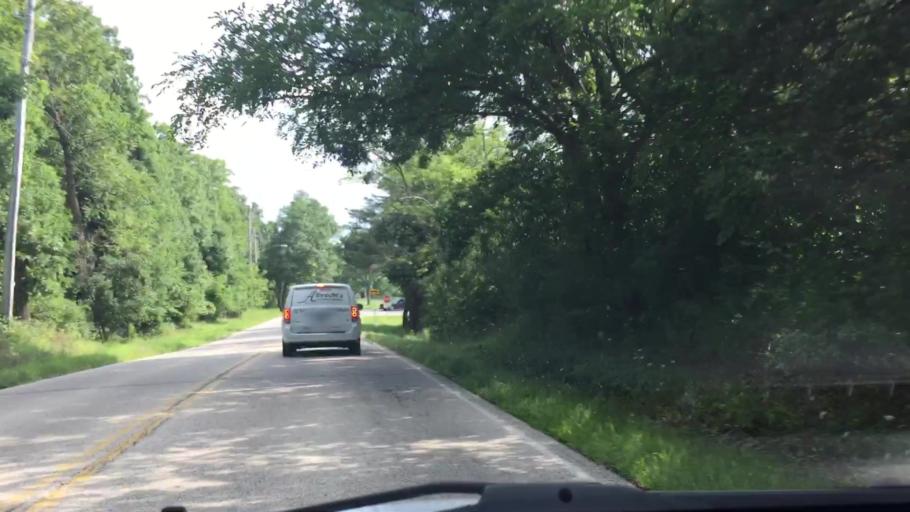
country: US
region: Wisconsin
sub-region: Waukesha County
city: Wales
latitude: 43.0416
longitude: -88.3496
